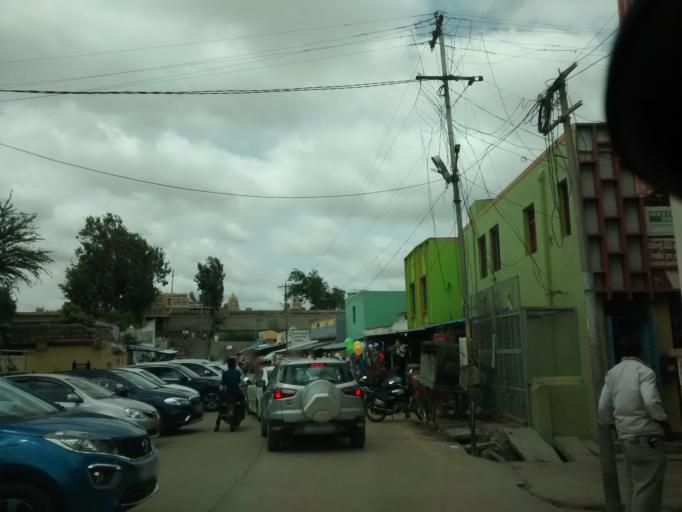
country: IN
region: Andhra Pradesh
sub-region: Anantapur
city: Hindupur
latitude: 13.8033
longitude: 77.6091
